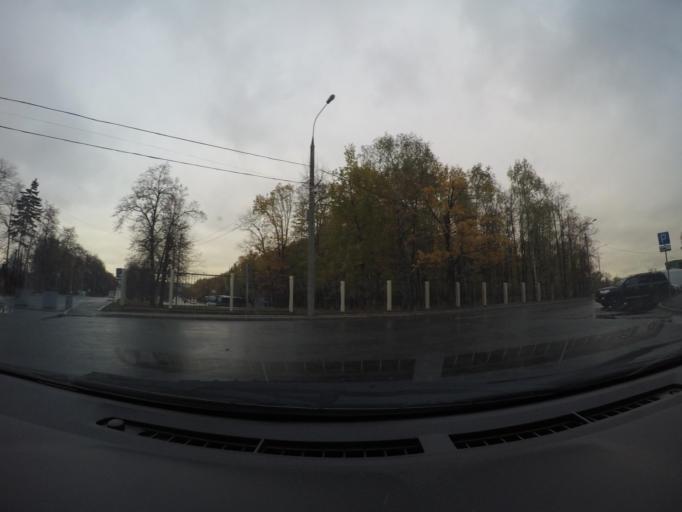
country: RU
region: Moskovskaya
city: Kastanayevo
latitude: 55.7309
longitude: 37.4932
